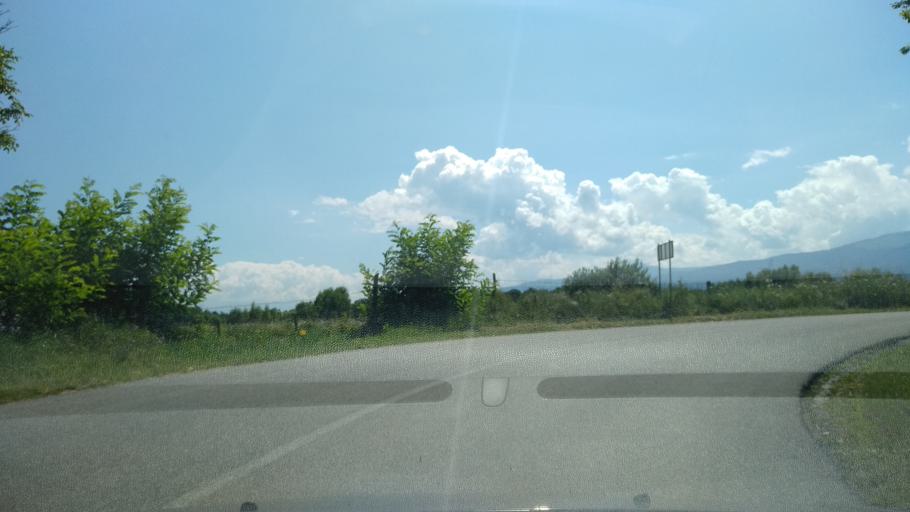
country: RO
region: Hunedoara
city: Salasu de Sus
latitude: 45.5297
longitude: 22.9673
